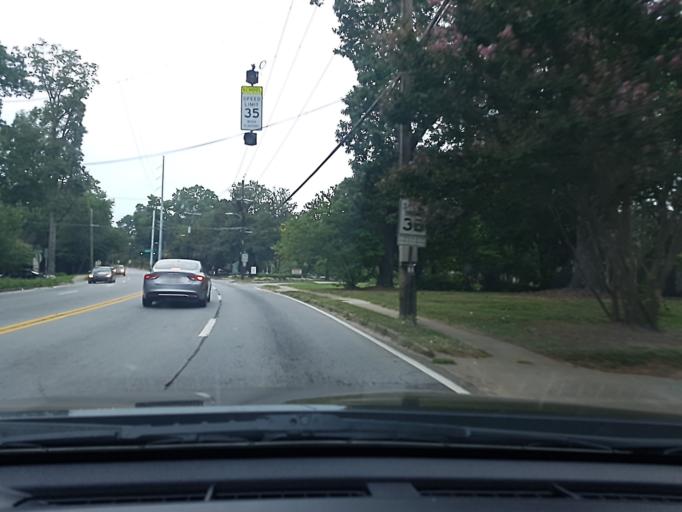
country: US
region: Georgia
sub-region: DeKalb County
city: North Decatur
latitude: 33.7924
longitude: -84.3133
